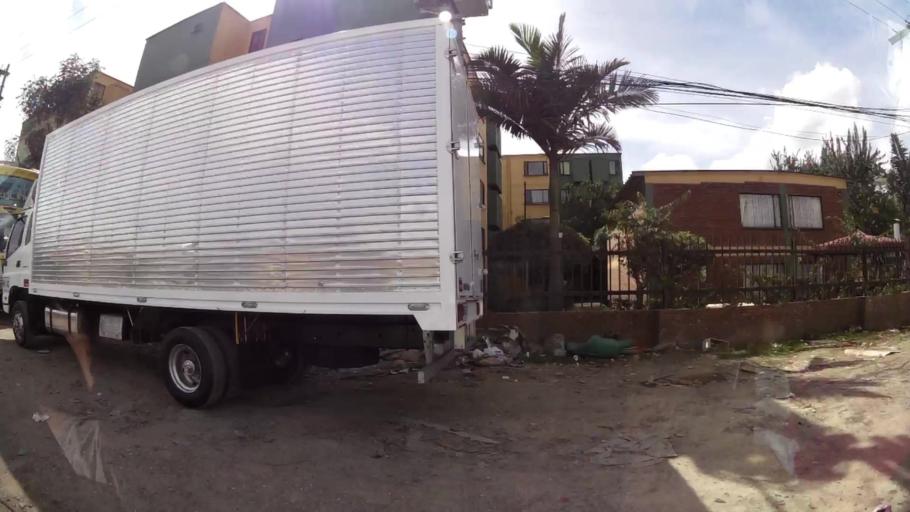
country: CO
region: Bogota D.C.
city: Bogota
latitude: 4.6505
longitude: -74.1372
